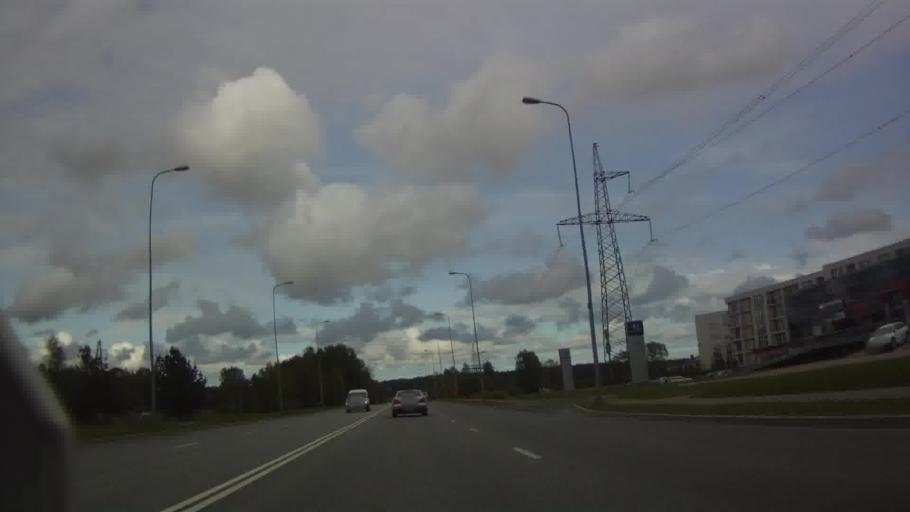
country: LV
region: Stopini
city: Ulbroka
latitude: 56.9573
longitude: 24.2419
